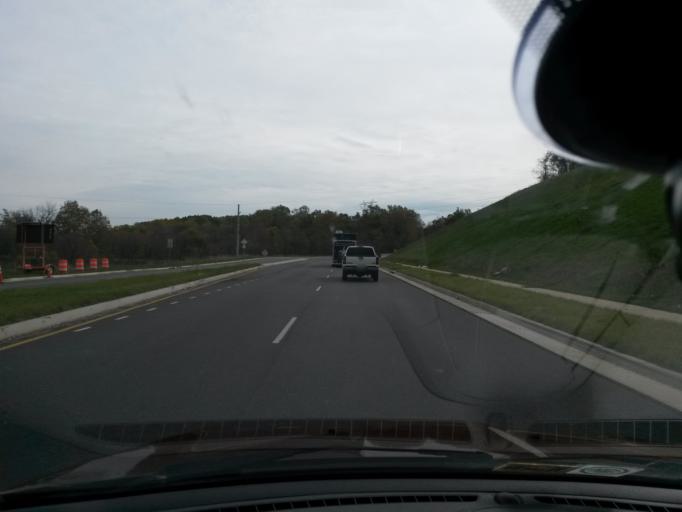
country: US
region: Virginia
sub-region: Botetourt County
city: Daleville
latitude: 37.3896
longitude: -79.8986
